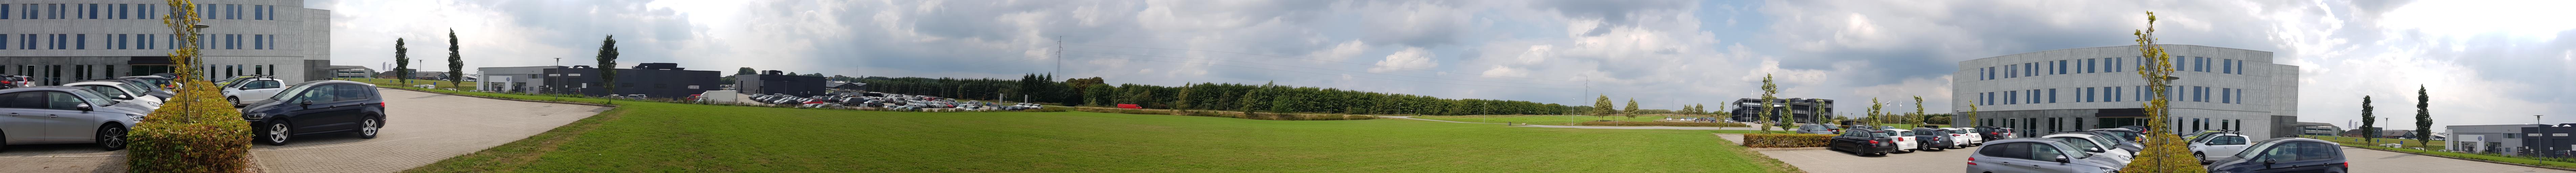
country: DK
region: Central Jutland
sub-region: Viborg Kommune
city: Viborg
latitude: 56.4648
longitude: 9.3725
